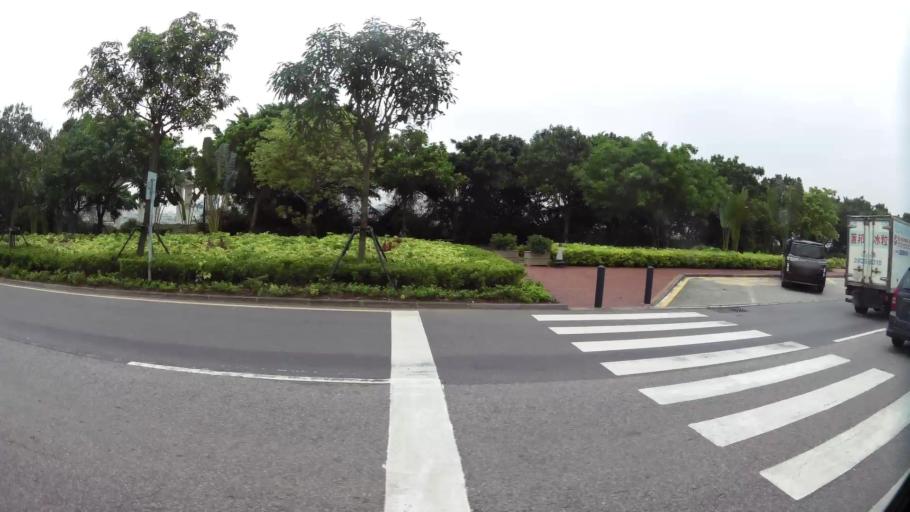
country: MO
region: Macau
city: Macau
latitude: 22.1409
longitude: 113.5524
